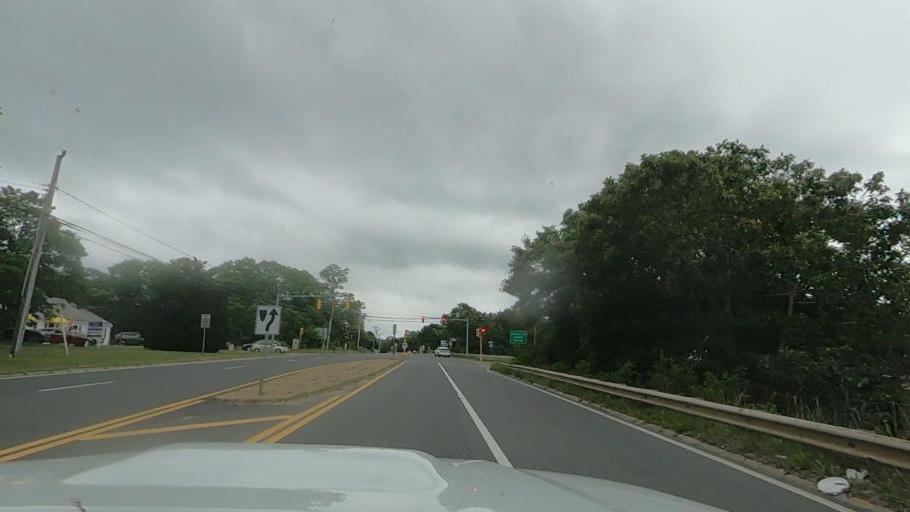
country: US
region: Massachusetts
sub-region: Barnstable County
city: Wellfleet
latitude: 41.9377
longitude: -70.0217
